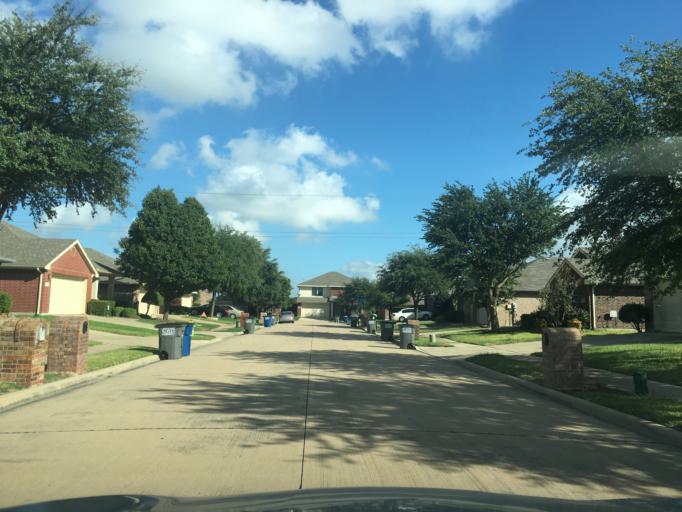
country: US
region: Texas
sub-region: Dallas County
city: Sachse
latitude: 32.9650
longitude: -96.5791
